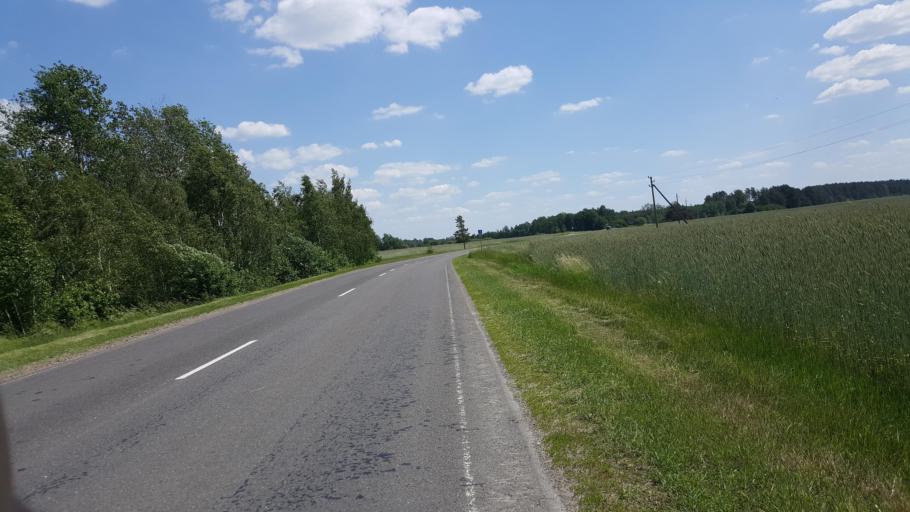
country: BY
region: Brest
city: Zhabinka
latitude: 52.2050
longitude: 24.0846
